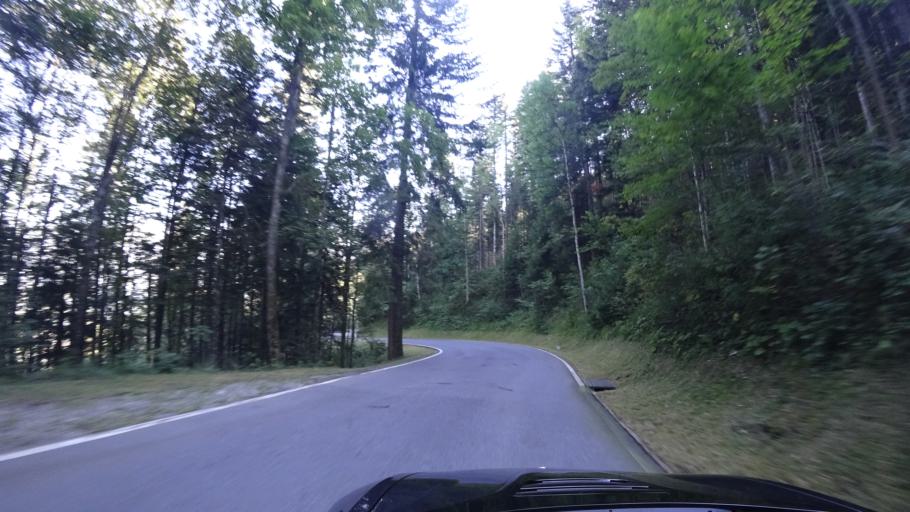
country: CH
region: Obwalden
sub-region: Obwalden
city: Giswil
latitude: 46.8292
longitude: 8.1307
